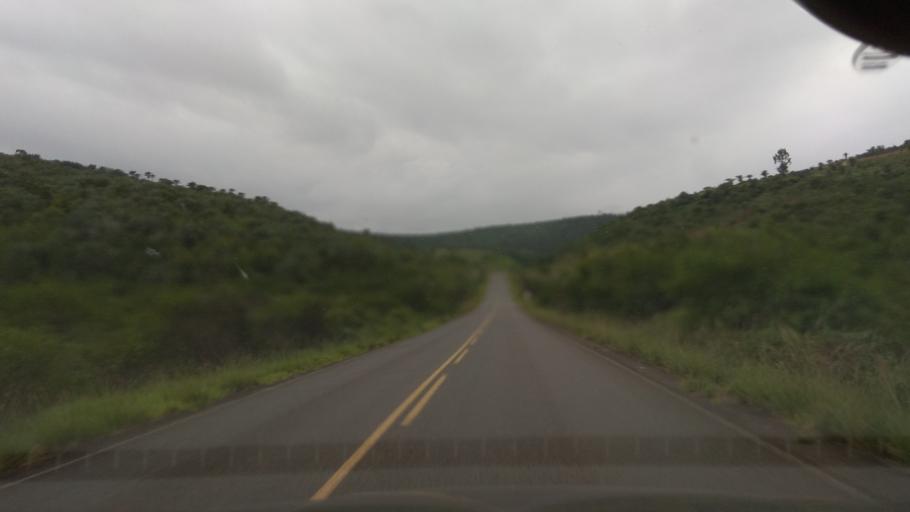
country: BR
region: Bahia
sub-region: Santa Ines
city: Santa Ines
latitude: -13.2692
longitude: -39.7986
